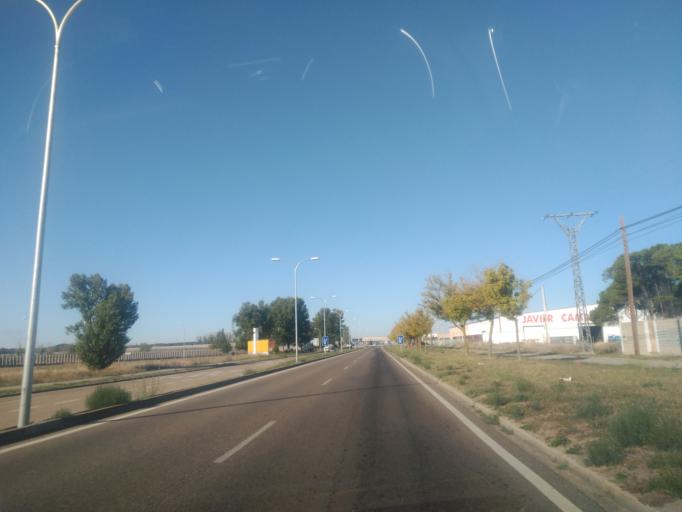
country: ES
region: Castille and Leon
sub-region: Provincia de Burgos
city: Villalba de Duero
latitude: 41.6654
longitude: -3.7217
